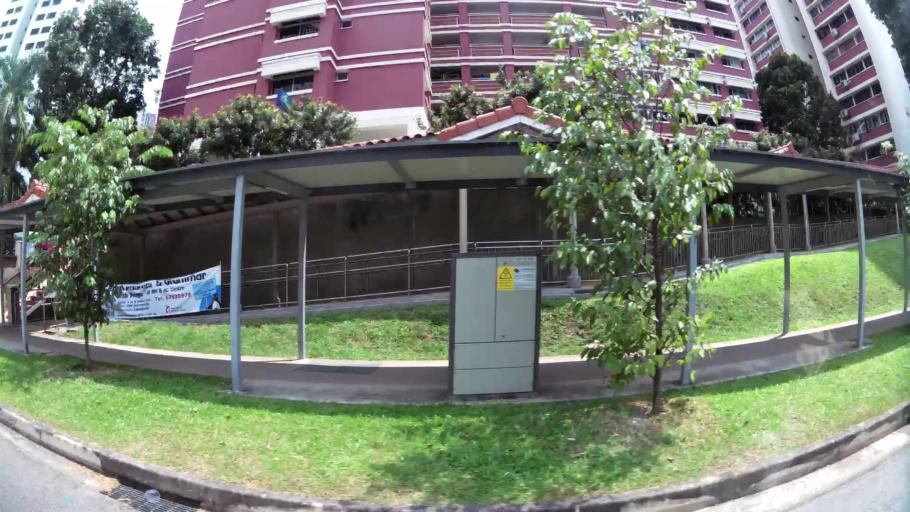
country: SG
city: Singapore
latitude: 1.2840
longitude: 103.8270
